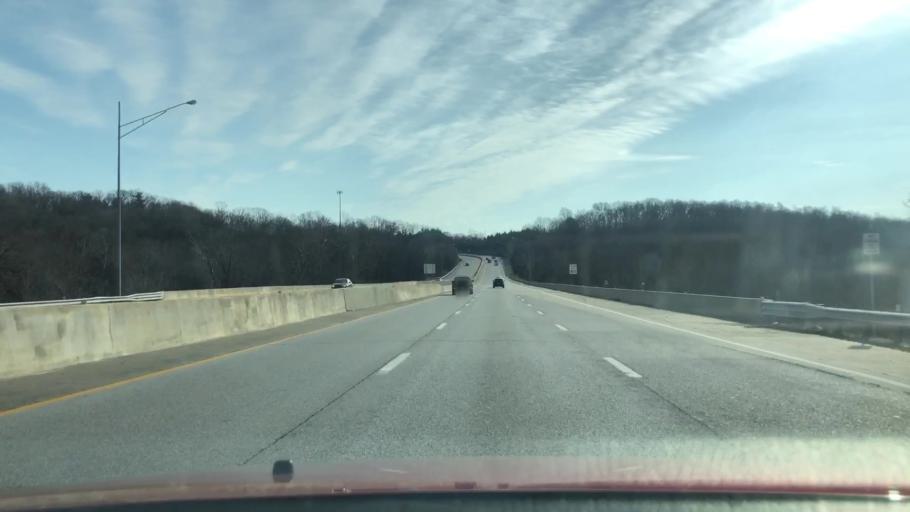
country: US
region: Missouri
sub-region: Christian County
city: Nixa
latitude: 37.1255
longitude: -93.2276
